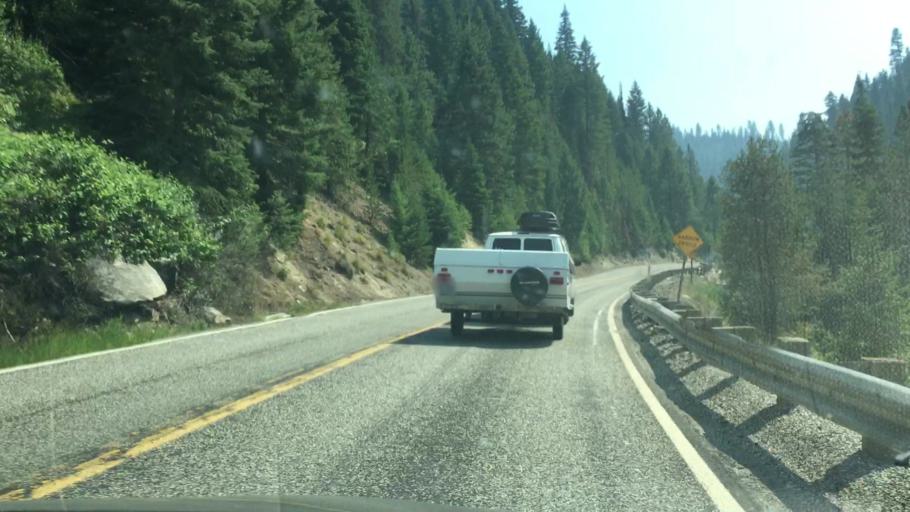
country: US
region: Idaho
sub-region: Valley County
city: Cascade
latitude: 44.3269
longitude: -116.0583
